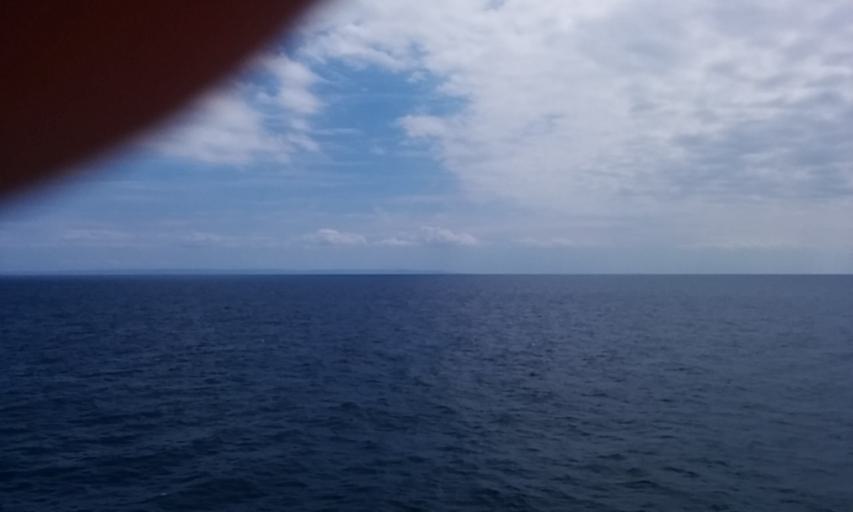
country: JP
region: Kagoshima
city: Nishinoomote
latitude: 30.5148
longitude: 130.6116
